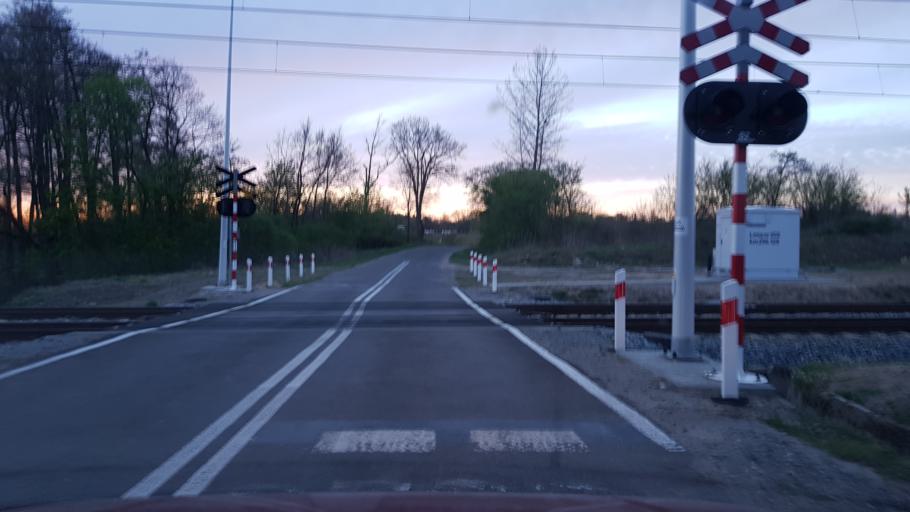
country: PL
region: West Pomeranian Voivodeship
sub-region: Powiat lobeski
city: Wegorzyno
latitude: 53.5122
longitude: 15.4480
